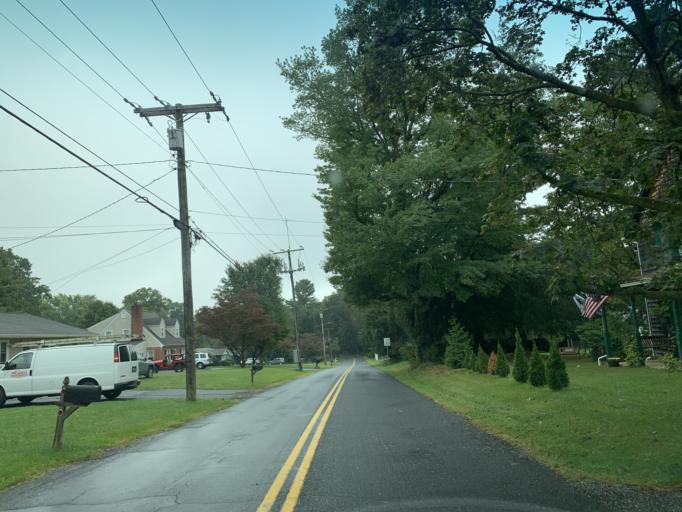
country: US
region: Maryland
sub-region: Harford County
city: Havre de Grace
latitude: 39.5729
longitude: -76.1485
